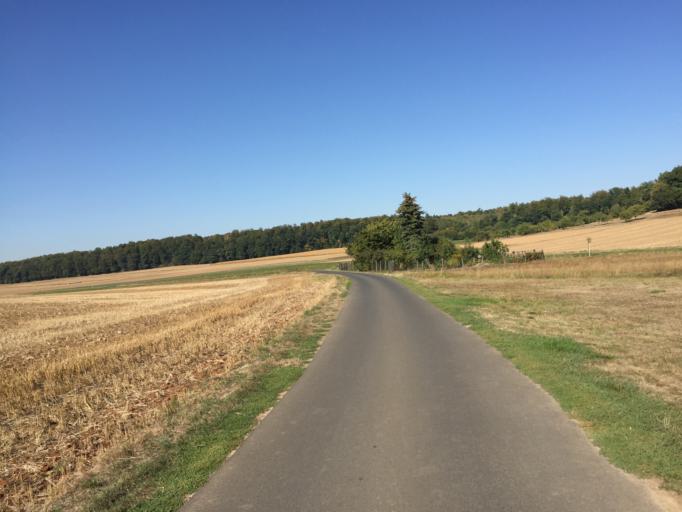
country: DE
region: Hesse
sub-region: Regierungsbezirk Darmstadt
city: Nidda
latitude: 50.4340
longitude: 8.9685
